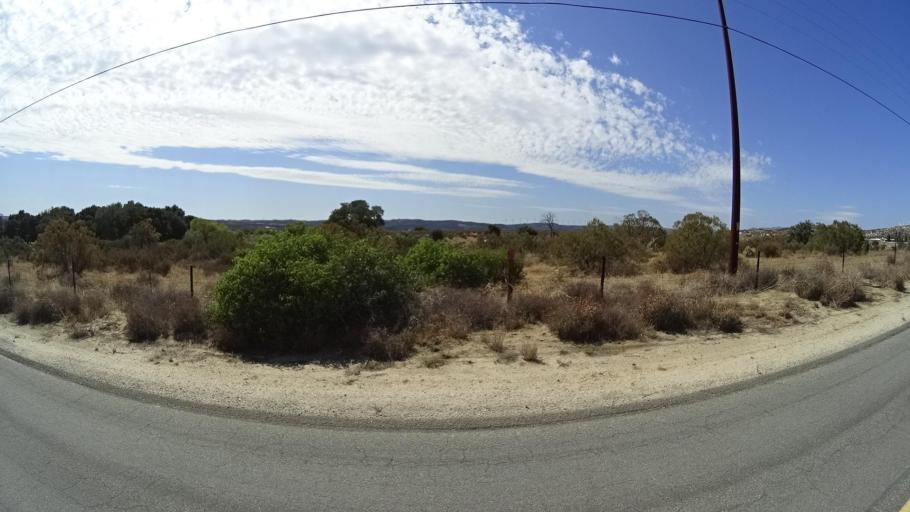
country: MX
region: Baja California
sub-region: Tecate
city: Cereso del Hongo
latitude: 32.6930
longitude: -116.2598
